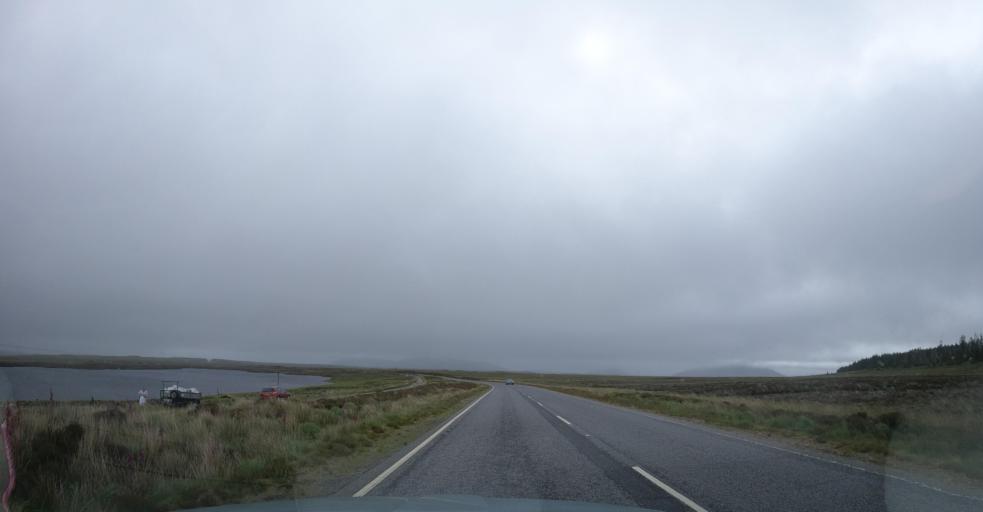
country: GB
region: Scotland
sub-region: Eilean Siar
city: Isle of North Uist
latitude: 57.5731
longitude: -7.2798
